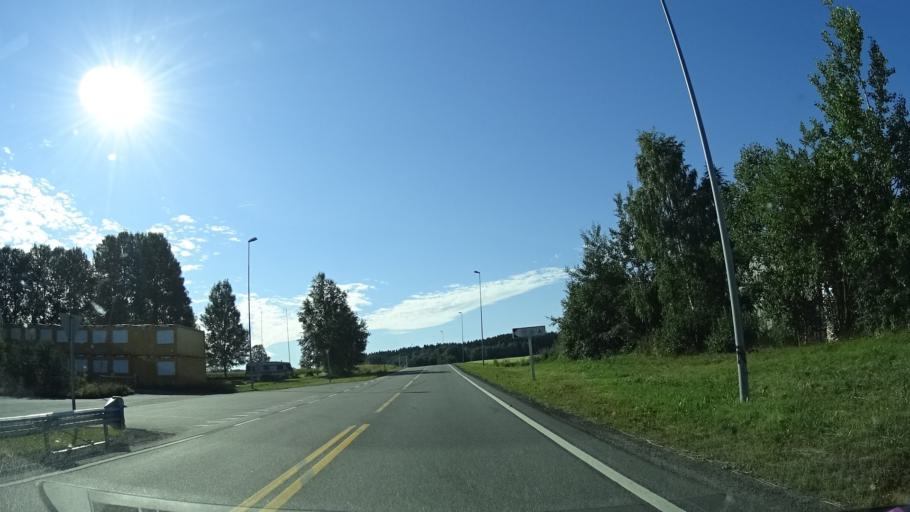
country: NO
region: Ostfold
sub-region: Eidsberg
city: Mysen
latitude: 59.5547
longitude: 11.3698
